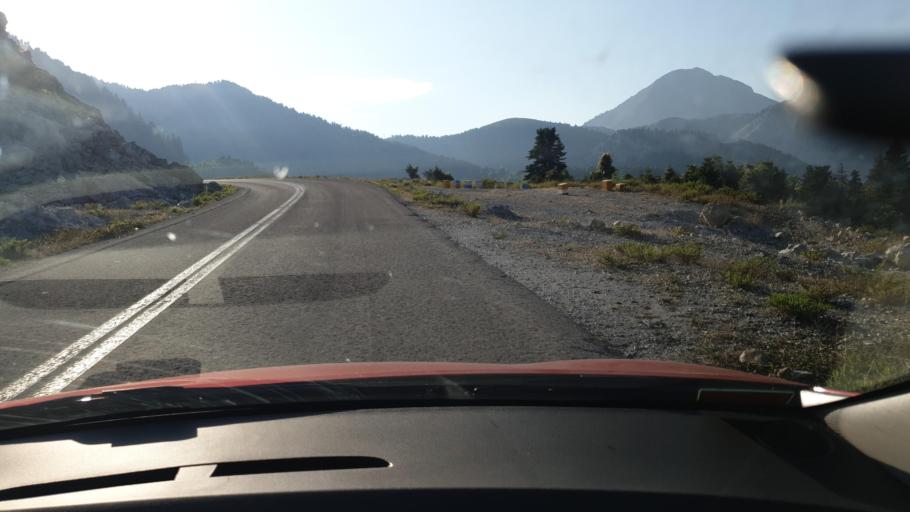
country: GR
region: Central Greece
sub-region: Nomos Evvoias
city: Yimnon
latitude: 38.5941
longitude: 23.8900
